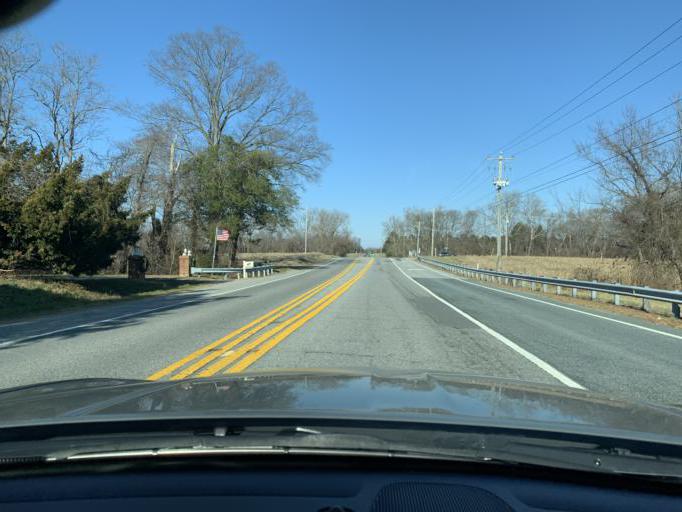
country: US
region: Maryland
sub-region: Queen Anne's County
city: Centreville
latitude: 39.0223
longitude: -76.0768
